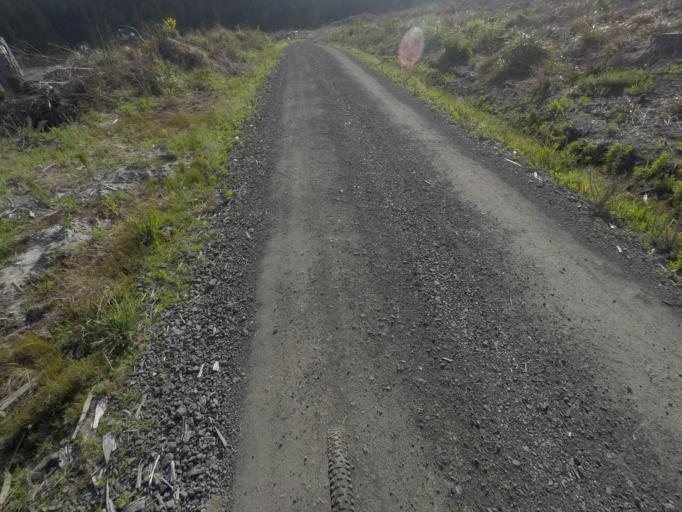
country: NZ
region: Auckland
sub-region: Auckland
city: Parakai
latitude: -36.7131
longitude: 174.5692
